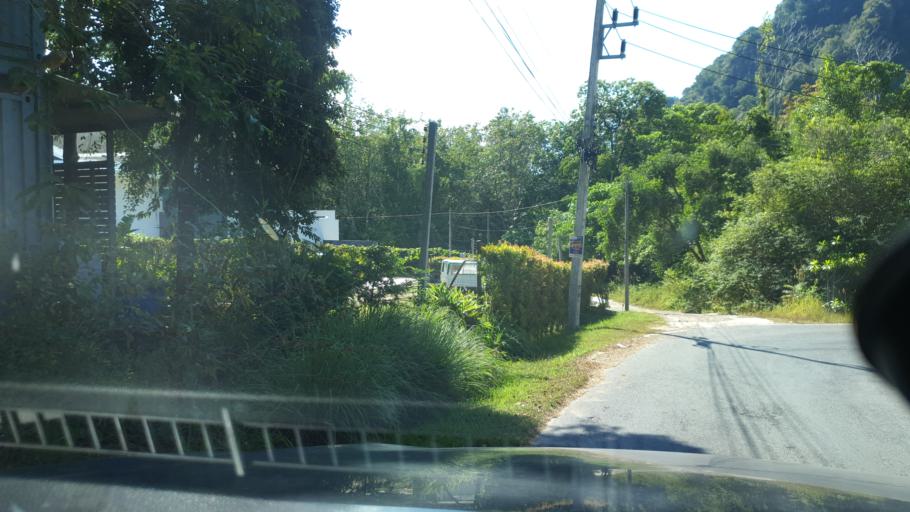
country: TH
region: Phangnga
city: Ban Ao Nang
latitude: 8.0276
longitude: 98.8559
